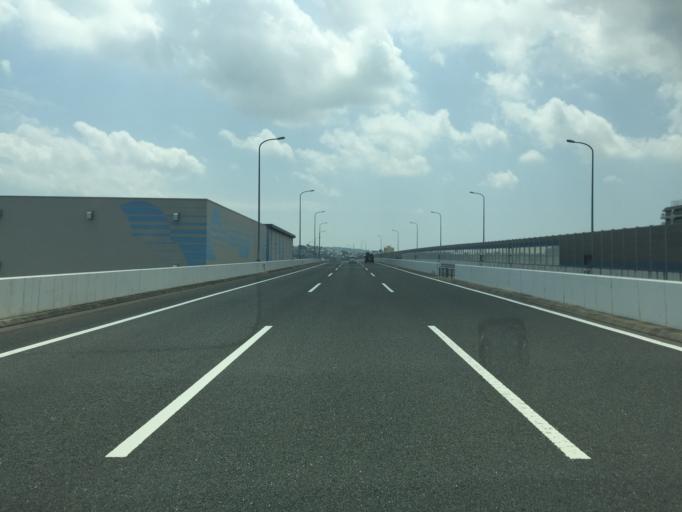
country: JP
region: Kanagawa
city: Yokohama
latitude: 35.3990
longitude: 139.6185
